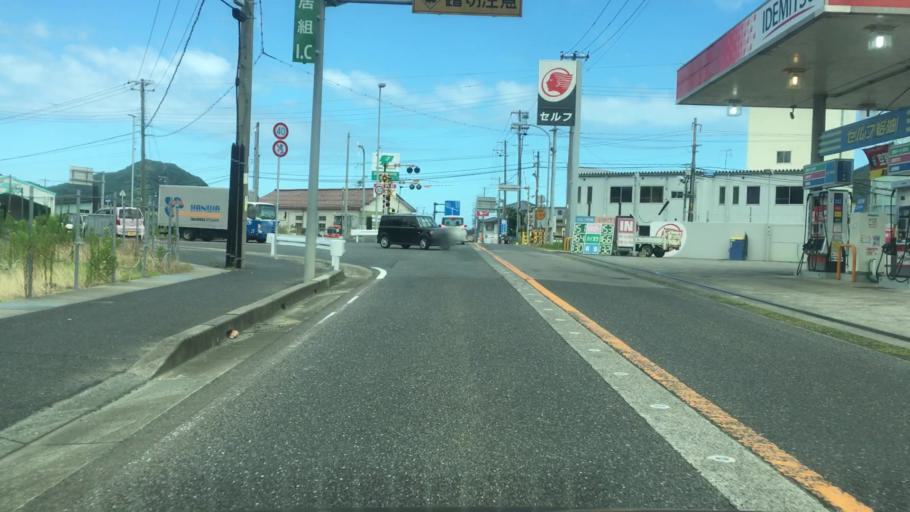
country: JP
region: Tottori
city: Tottori
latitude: 35.6188
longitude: 134.4621
